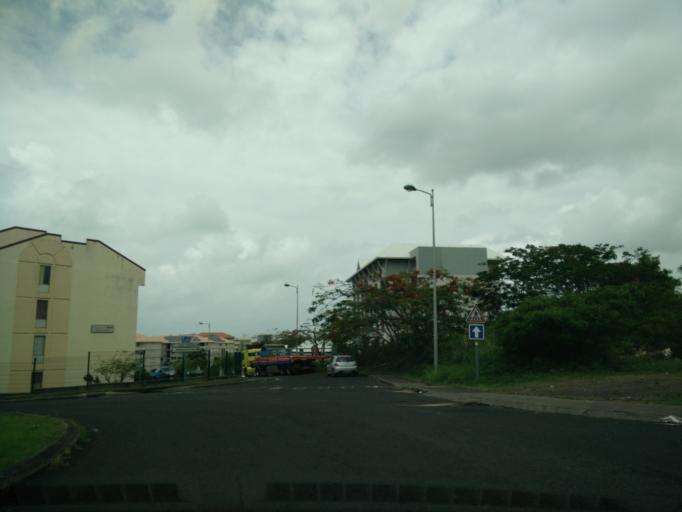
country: MQ
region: Martinique
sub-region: Martinique
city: Fort-de-France
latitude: 14.6030
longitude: -61.0424
